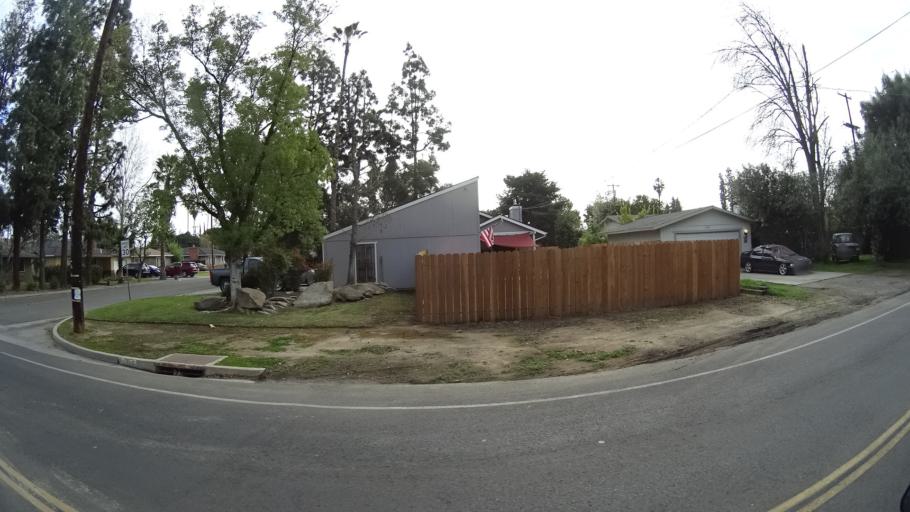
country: US
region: California
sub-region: Fresno County
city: Fresno
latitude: 36.7903
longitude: -119.7996
